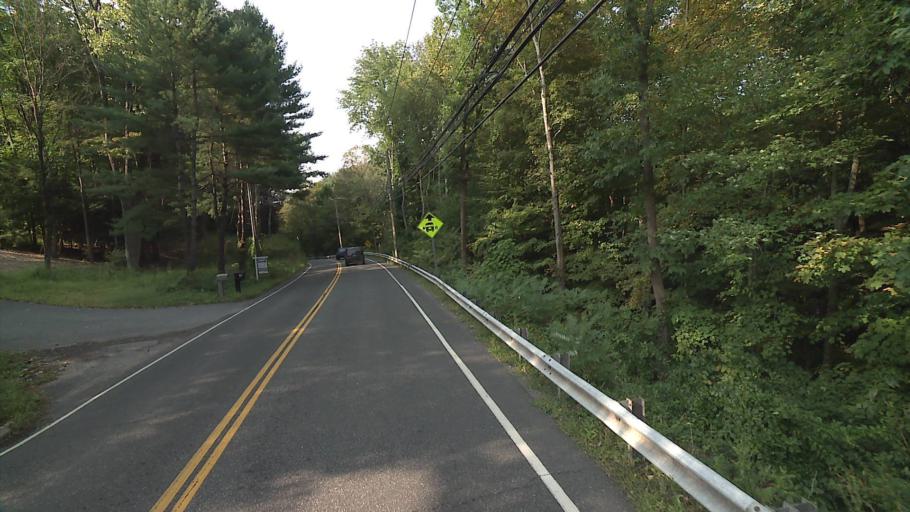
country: US
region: Connecticut
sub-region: Fairfield County
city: Newtown
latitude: 41.4279
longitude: -73.2805
